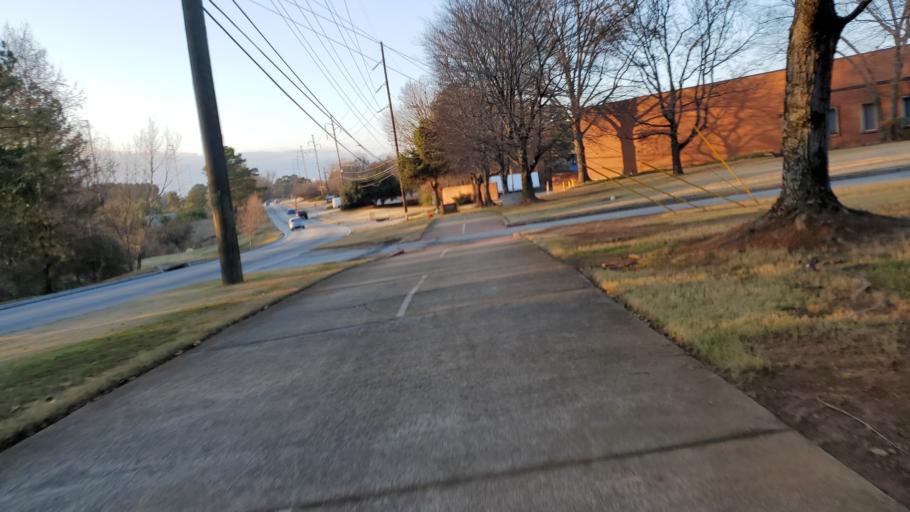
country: US
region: Georgia
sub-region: DeKalb County
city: Stone Mountain
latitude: 33.8223
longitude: -84.1874
